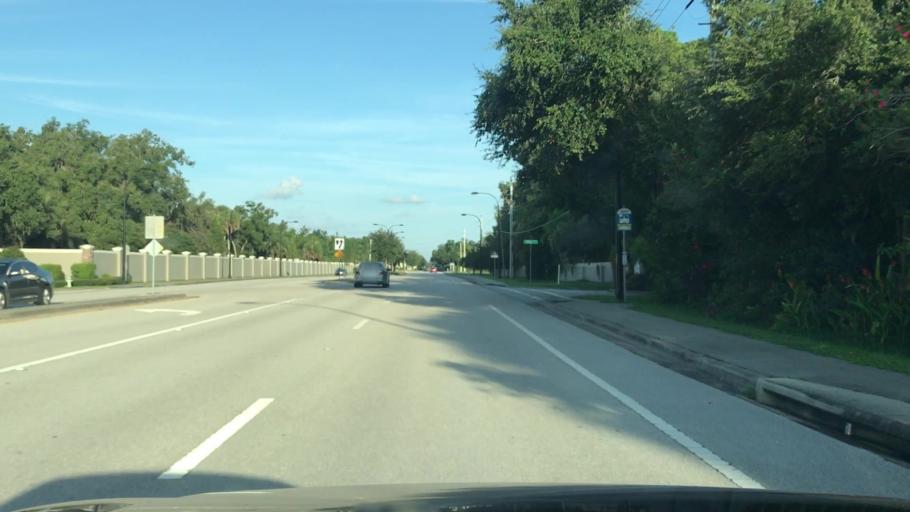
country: US
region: Florida
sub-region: Sarasota County
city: Fruitville
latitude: 27.3231
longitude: -82.4694
